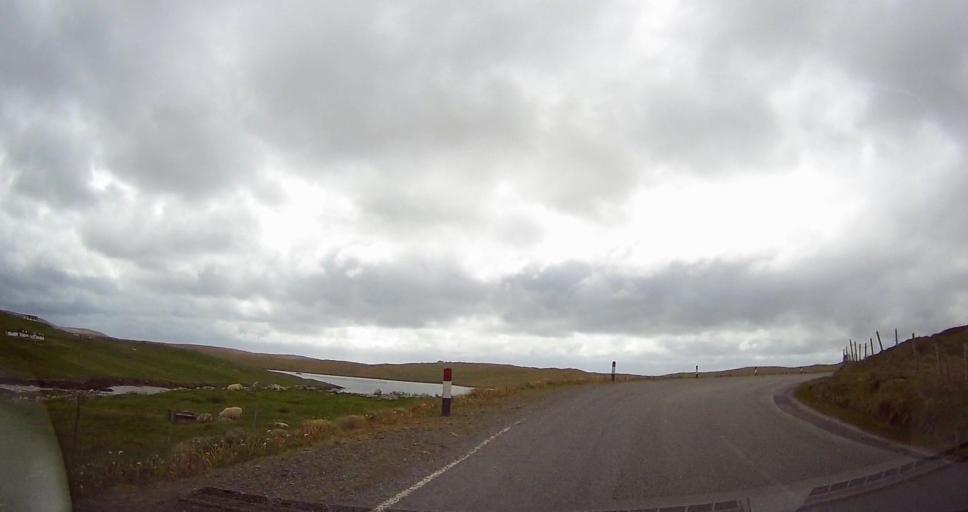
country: GB
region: Scotland
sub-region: Shetland Islands
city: Sandwick
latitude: 60.2438
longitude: -1.5126
